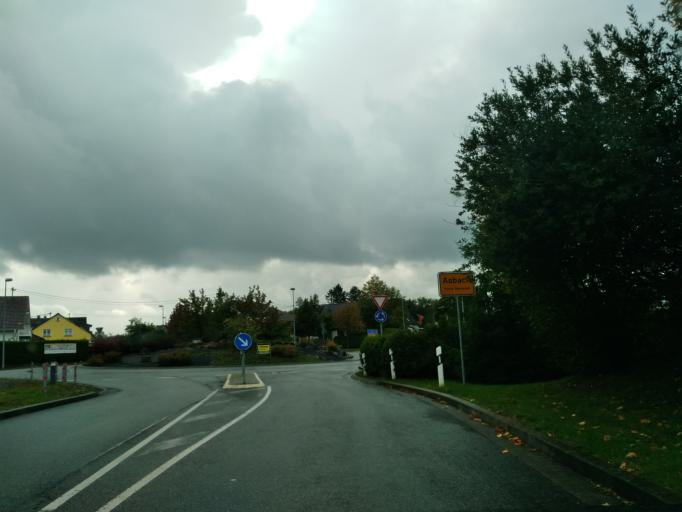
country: DE
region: Rheinland-Pfalz
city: Asbach
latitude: 50.6691
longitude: 7.4332
